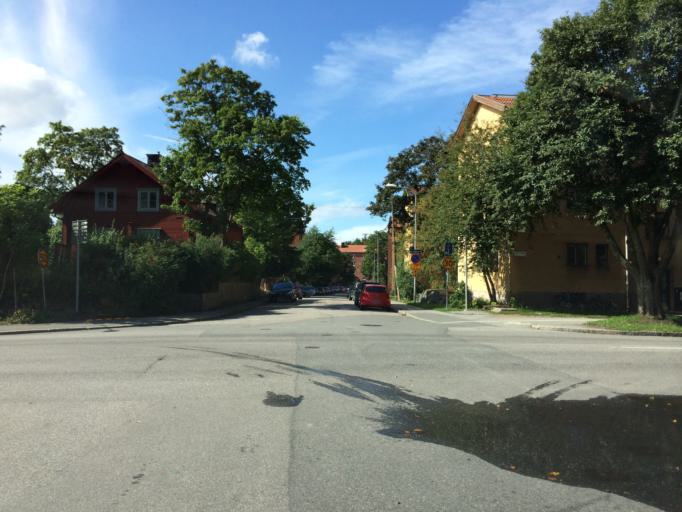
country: SE
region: Stockholm
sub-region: Huddinge Kommun
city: Huddinge
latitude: 59.2908
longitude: 17.9916
